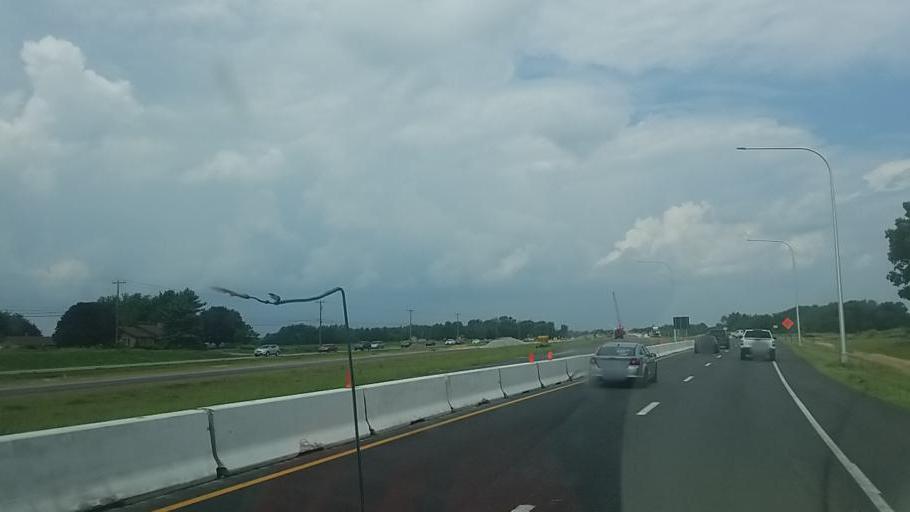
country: US
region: Delaware
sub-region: Kent County
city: Riverview
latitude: 39.0341
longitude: -75.4574
